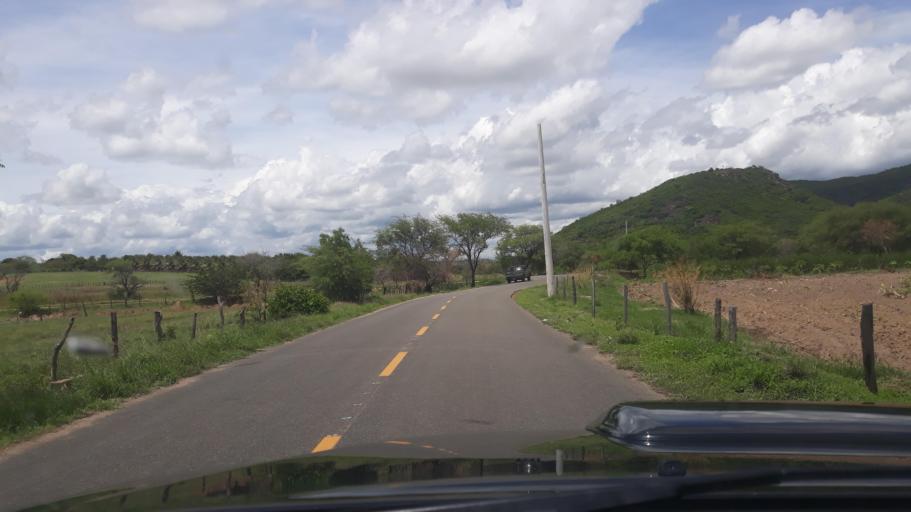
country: BR
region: Bahia
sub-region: Guanambi
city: Guanambi
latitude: -14.2768
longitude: -42.7124
